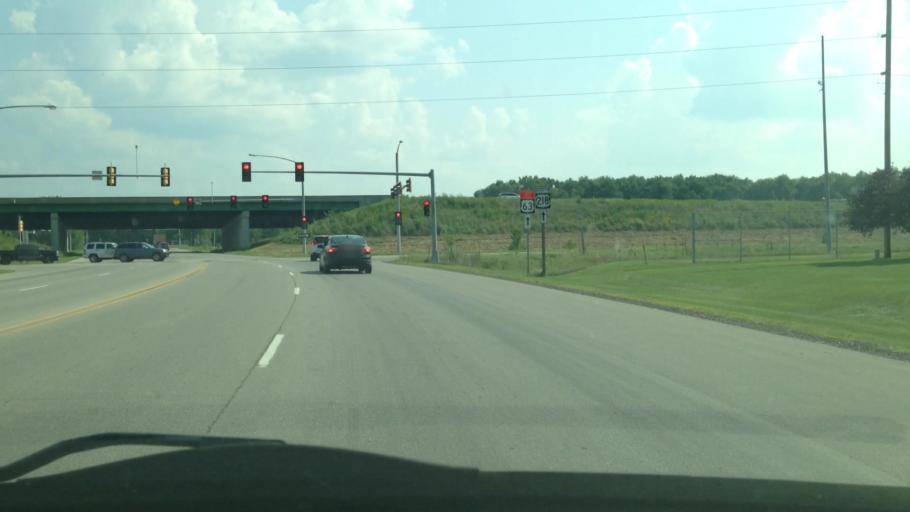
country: US
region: Iowa
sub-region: Black Hawk County
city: Cedar Falls
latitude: 42.5406
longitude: -92.3953
